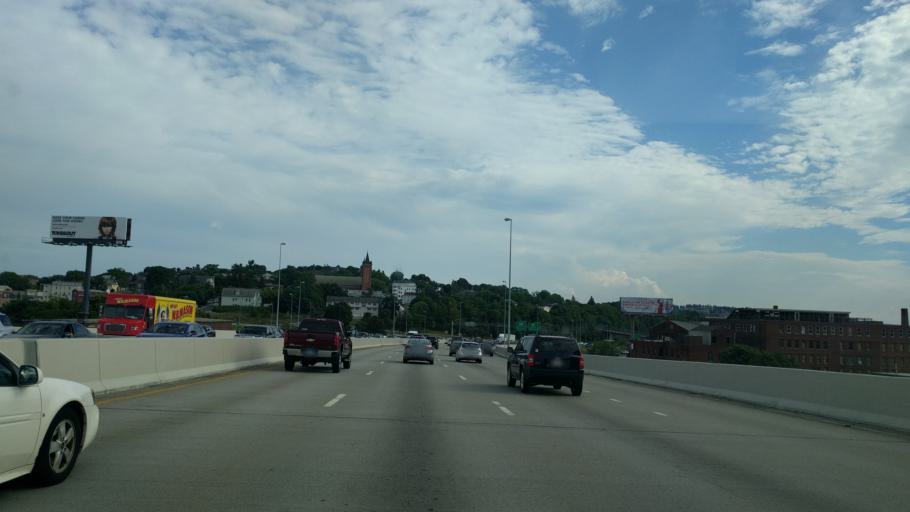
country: US
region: Massachusetts
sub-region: Worcester County
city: Worcester
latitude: 42.2604
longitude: -71.7935
